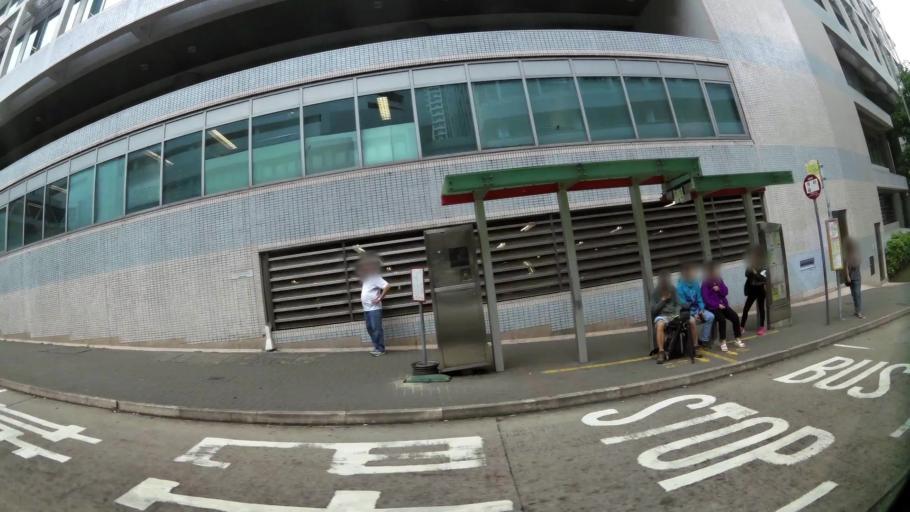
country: HK
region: Kowloon City
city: Kowloon
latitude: 22.3156
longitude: 114.1812
